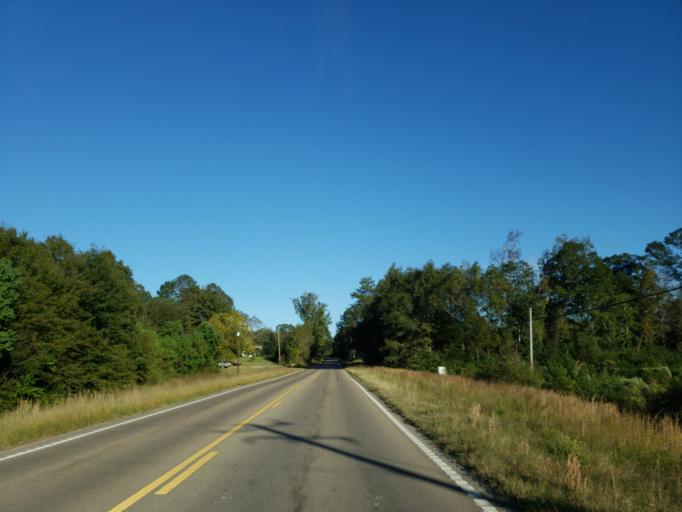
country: US
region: Mississippi
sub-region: Perry County
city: Richton
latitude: 31.3564
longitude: -88.9187
